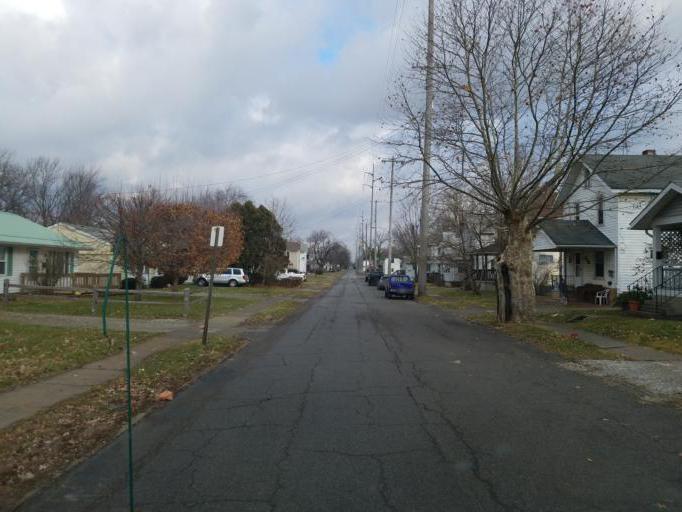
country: US
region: Ohio
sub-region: Marion County
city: Marion
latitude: 40.5793
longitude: -83.1455
